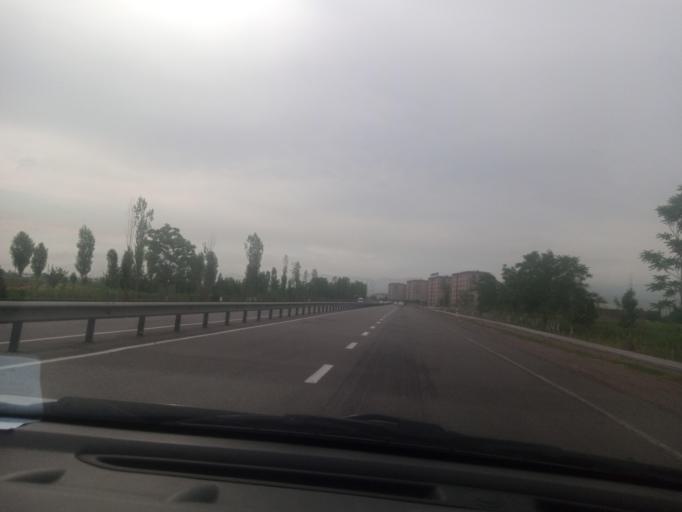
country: UZ
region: Toshkent
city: Ohangaron
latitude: 40.9165
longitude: 69.6047
